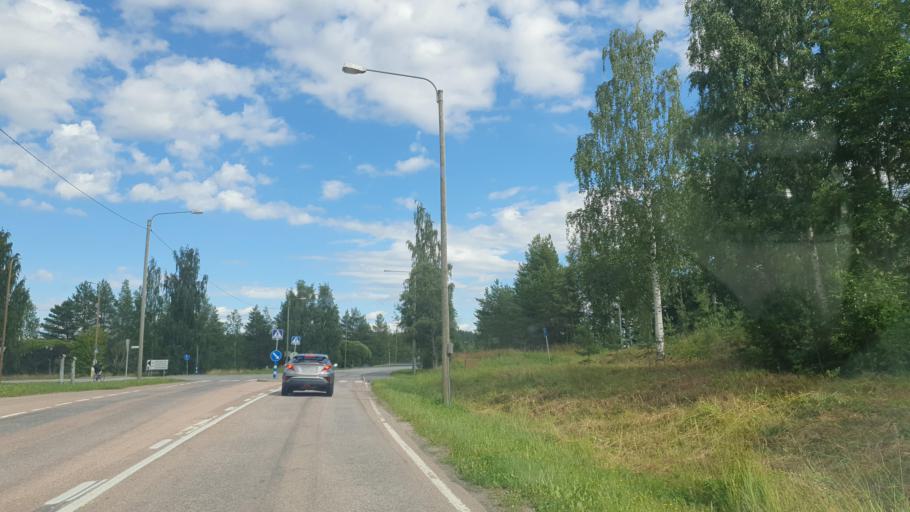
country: FI
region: Central Finland
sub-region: Jyvaeskylae
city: Saeynaetsalo
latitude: 62.1388
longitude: 25.7417
